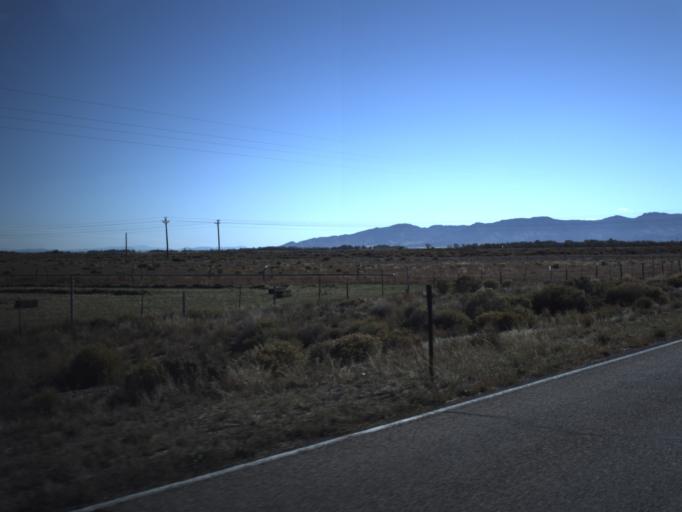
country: US
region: Utah
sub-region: Washington County
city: Enterprise
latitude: 37.7234
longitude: -113.6950
